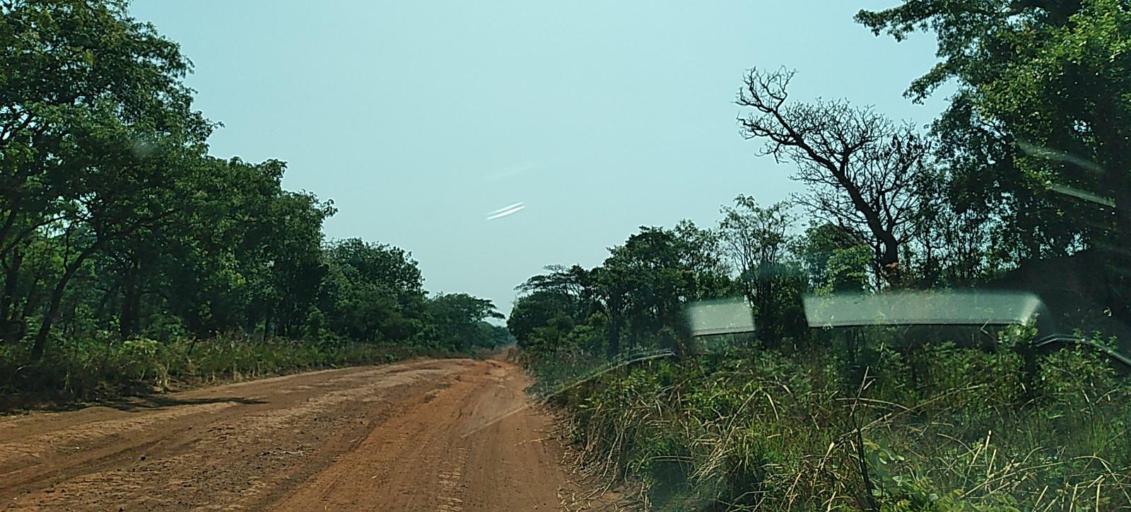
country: ZM
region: North-Western
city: Kansanshi
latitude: -12.0089
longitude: 26.5133
